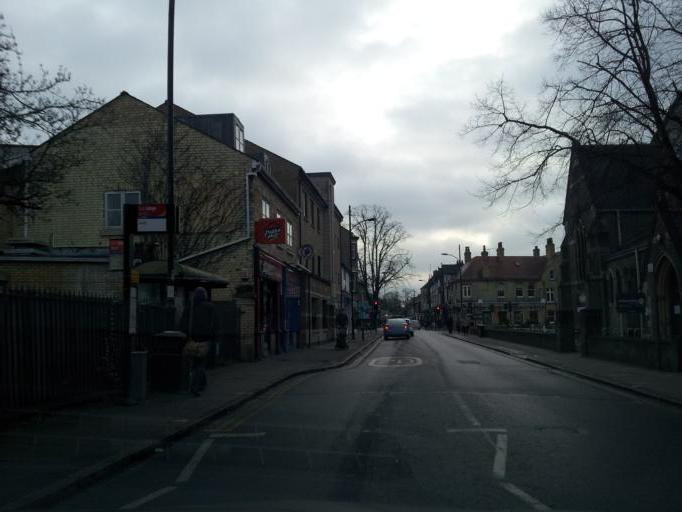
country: GB
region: England
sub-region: Cambridgeshire
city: Cambridge
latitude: 52.2000
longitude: 0.1373
